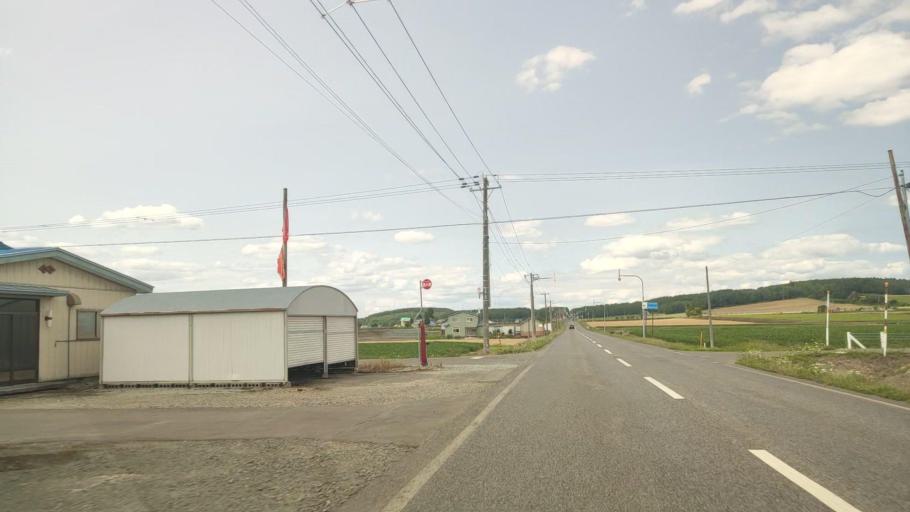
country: JP
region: Hokkaido
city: Nayoro
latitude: 44.2307
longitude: 142.4157
